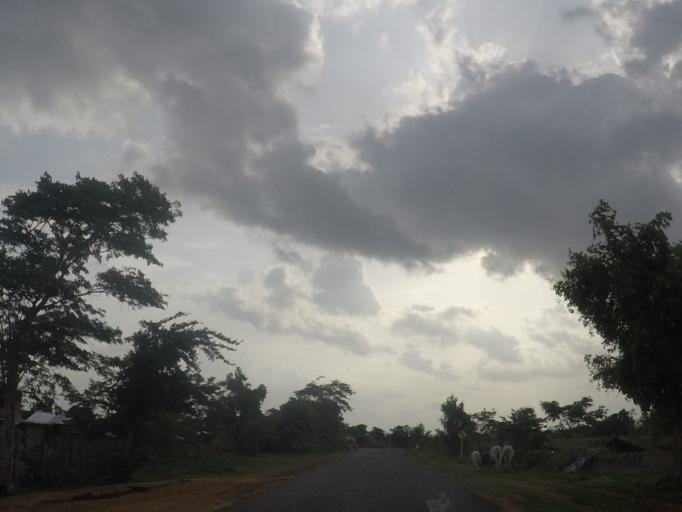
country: MM
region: Mandalay
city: Meiktila
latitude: 20.5203
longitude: 95.6388
